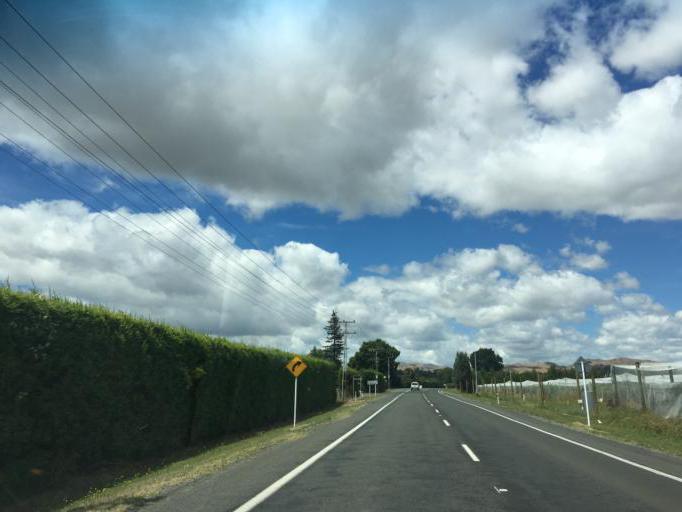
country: NZ
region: Hawke's Bay
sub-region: Hastings District
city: Hastings
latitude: -39.6547
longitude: 176.8873
